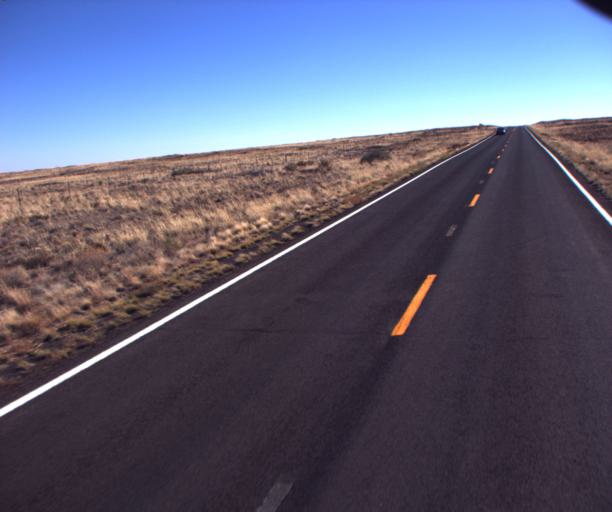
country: US
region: Arizona
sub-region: Coconino County
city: Tuba City
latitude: 35.9744
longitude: -110.9725
